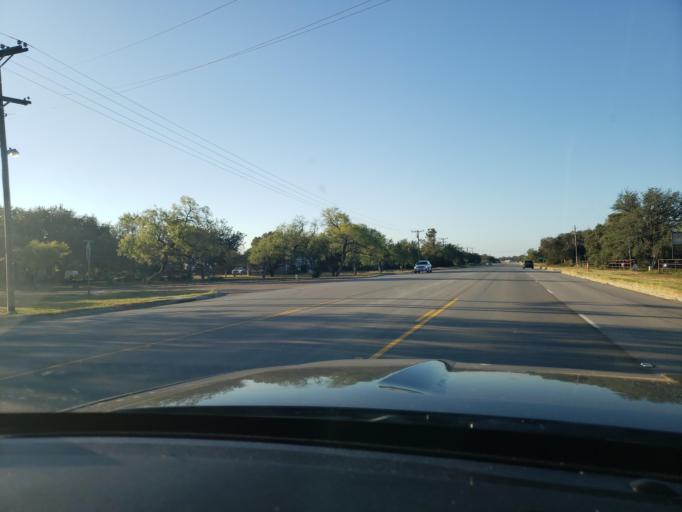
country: US
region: Texas
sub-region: Bee County
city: Beeville
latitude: 28.4311
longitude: -97.7148
